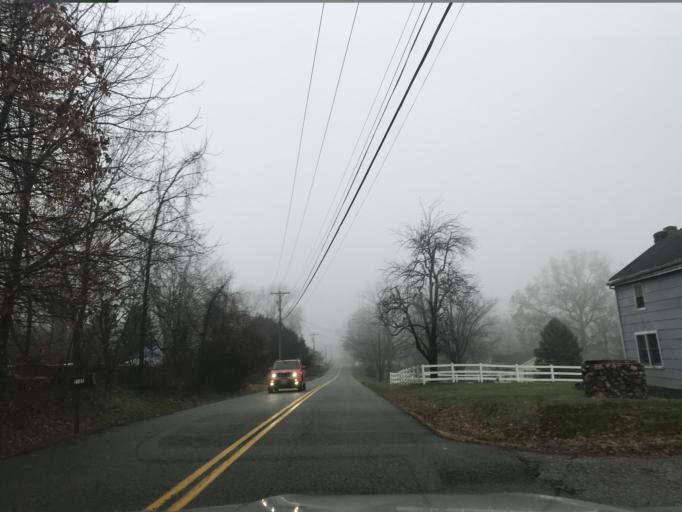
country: US
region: Maryland
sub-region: Harford County
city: South Bel Air
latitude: 39.5669
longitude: -76.3183
